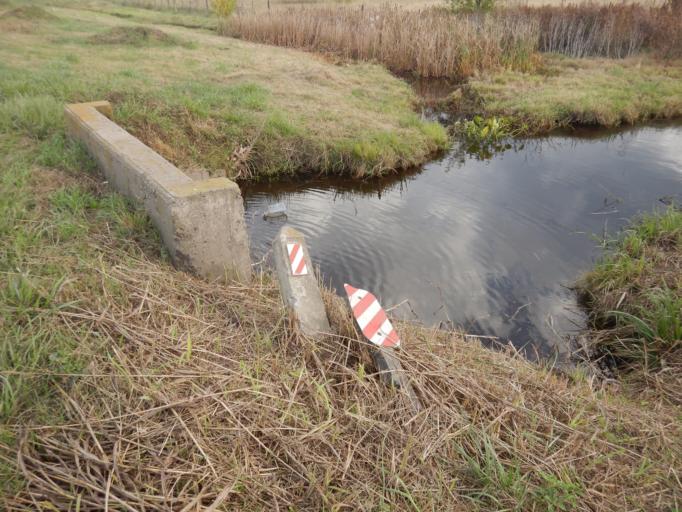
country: AR
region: Santa Fe
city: Roldan
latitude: -32.8995
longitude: -60.9420
